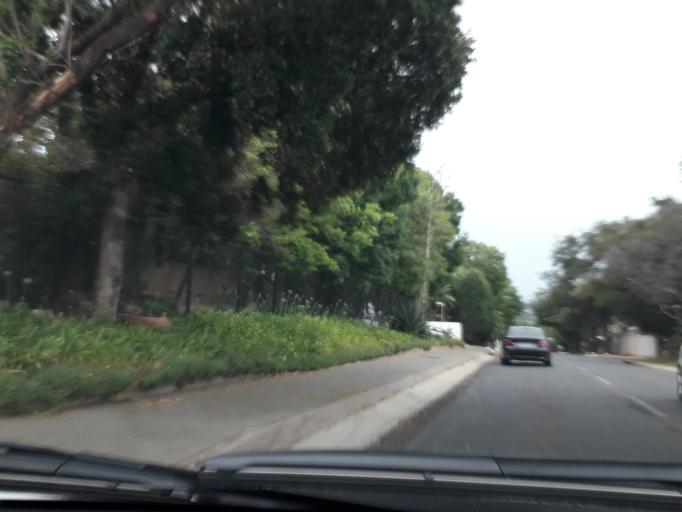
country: ZA
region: Gauteng
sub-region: City of Johannesburg Metropolitan Municipality
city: Johannesburg
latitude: -26.0938
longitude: 28.0352
